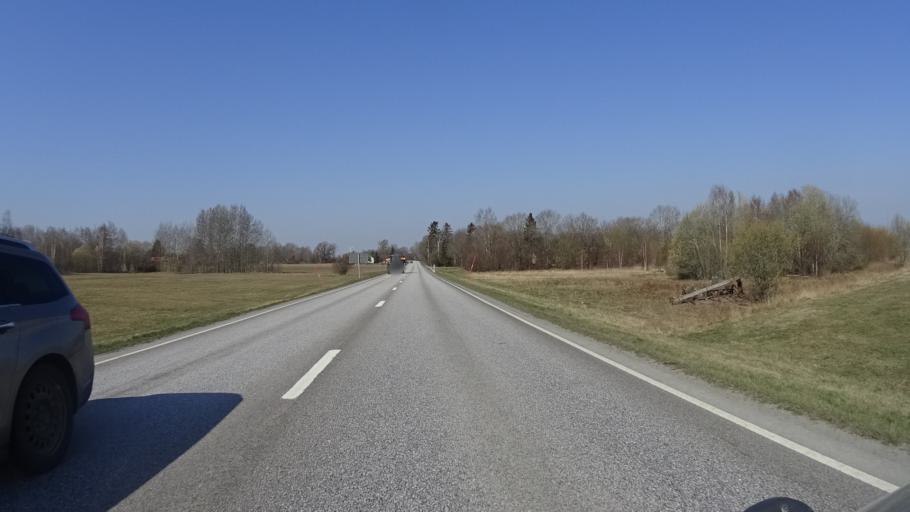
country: SE
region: OEstergoetland
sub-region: Mjolby Kommun
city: Mantorp
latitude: 58.3751
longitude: 15.2829
